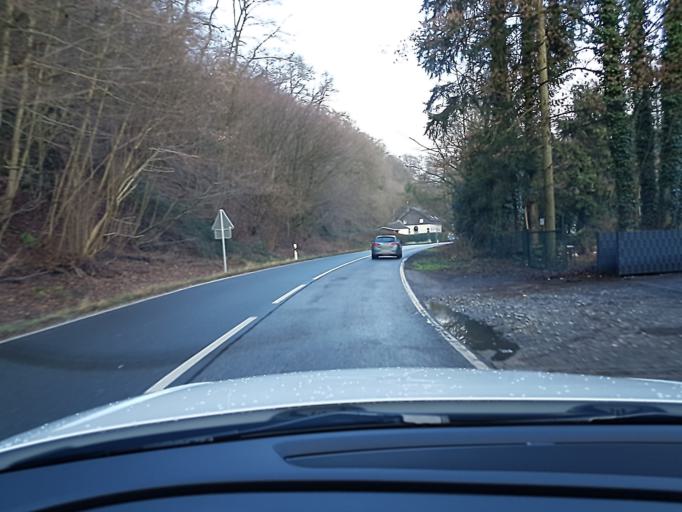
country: DE
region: North Rhine-Westphalia
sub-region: Regierungsbezirk Dusseldorf
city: Heiligenhaus
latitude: 51.3747
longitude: 6.9601
